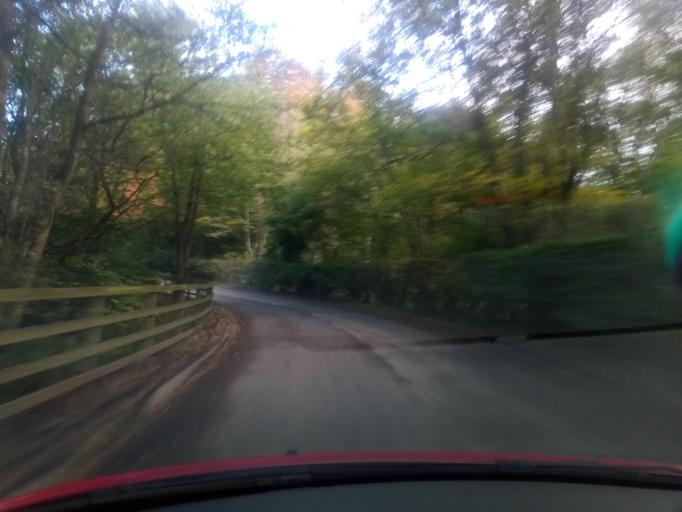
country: GB
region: Scotland
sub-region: The Scottish Borders
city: Jedburgh
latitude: 55.3832
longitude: -2.6427
